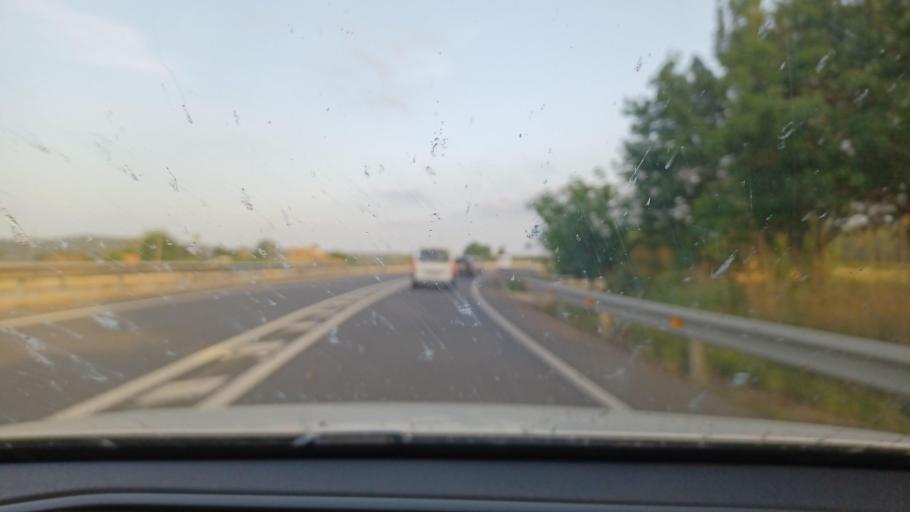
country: ES
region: Catalonia
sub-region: Provincia de Tarragona
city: Amposta
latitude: 40.7467
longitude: 0.5590
